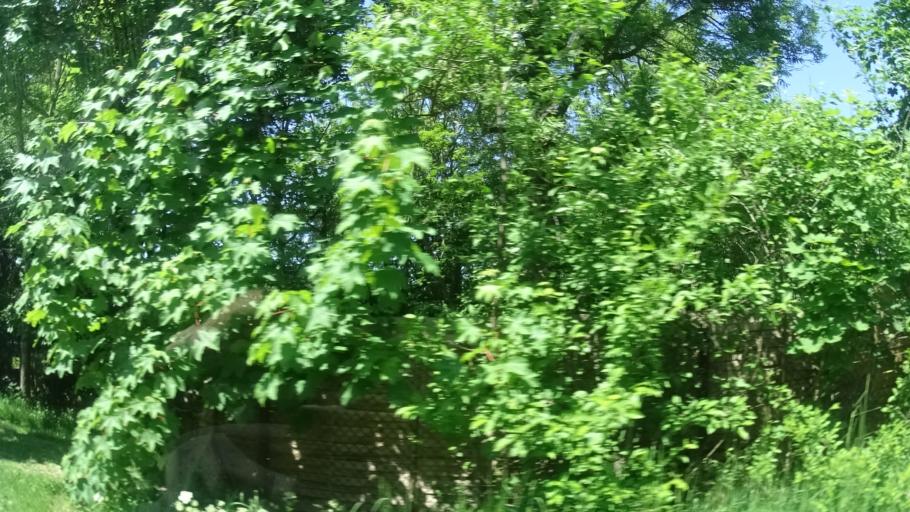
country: DE
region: Thuringia
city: Arnstadt
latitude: 50.8258
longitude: 10.9354
